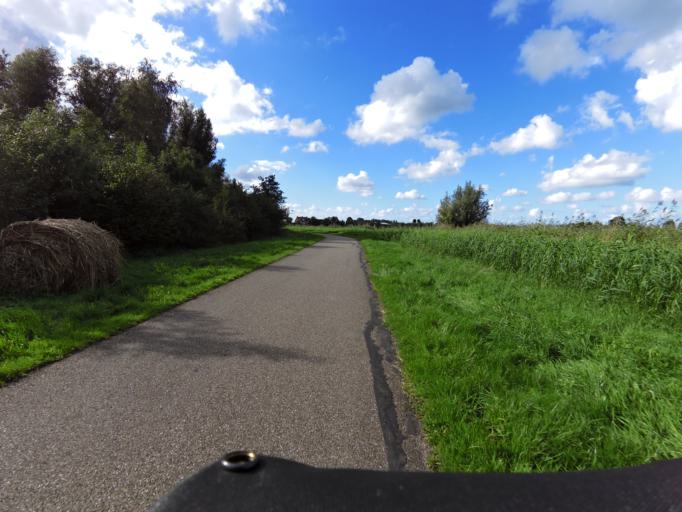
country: NL
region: South Holland
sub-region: Gemeente Vlaardingen
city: Vlaardingen
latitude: 51.9422
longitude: 4.3280
